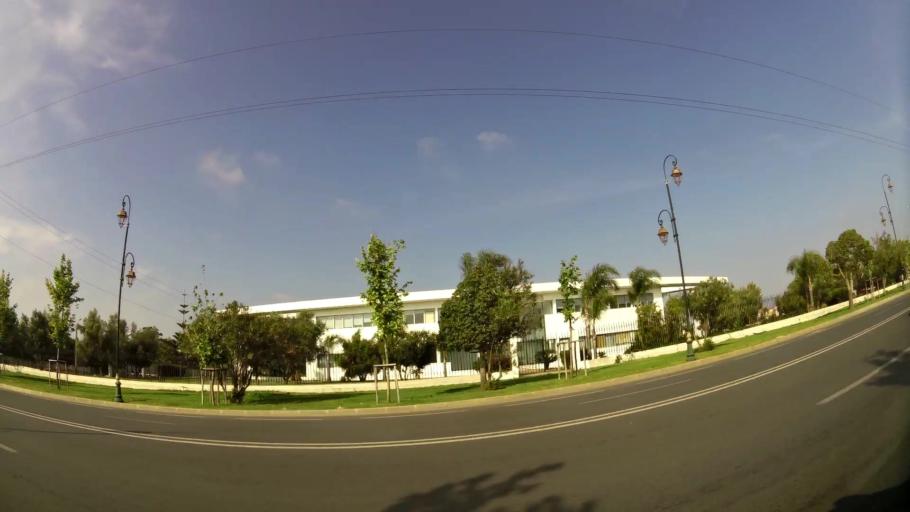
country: MA
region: Rabat-Sale-Zemmour-Zaer
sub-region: Rabat
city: Rabat
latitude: 33.9431
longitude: -6.8078
